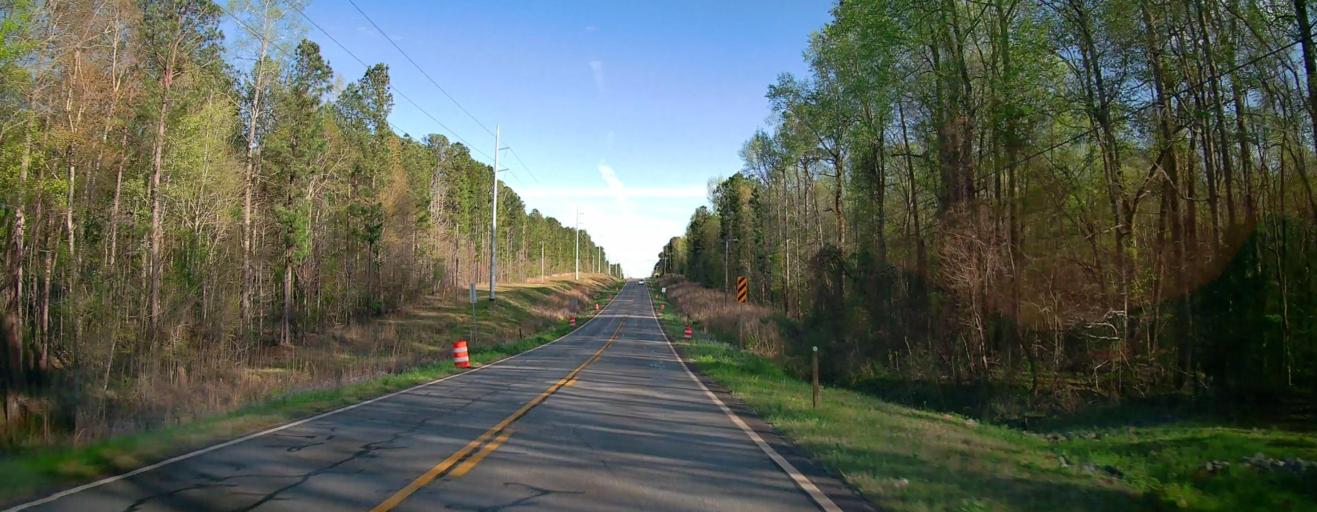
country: US
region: Georgia
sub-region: Baldwin County
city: Milledgeville
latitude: 33.1352
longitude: -83.3250
